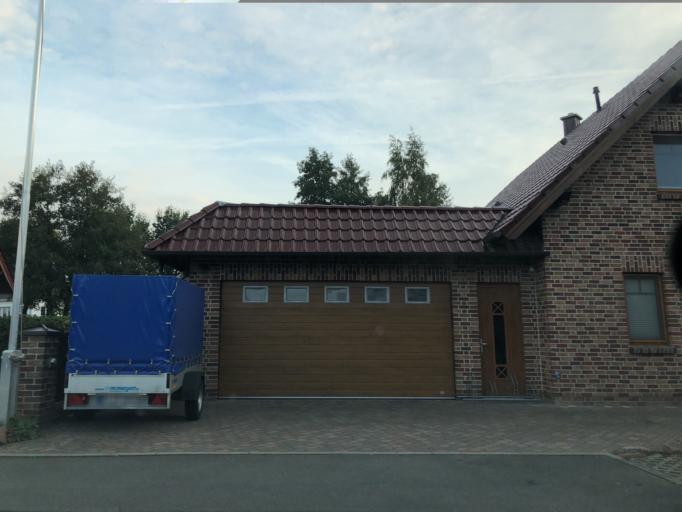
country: DE
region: Lower Saxony
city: Papenburg
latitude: 53.0738
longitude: 7.4529
